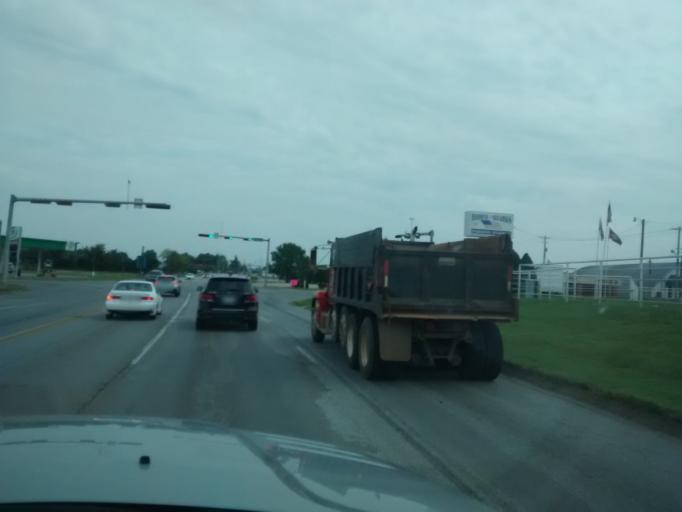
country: US
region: Arkansas
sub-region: Washington County
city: Springdale
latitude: 36.1839
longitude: -94.1162
